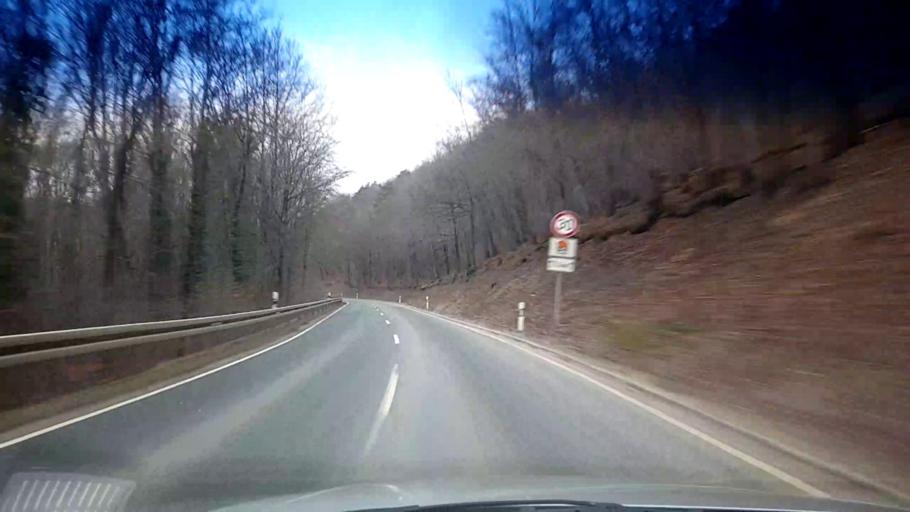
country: DE
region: Bavaria
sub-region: Upper Franconia
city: Wattendorf
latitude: 50.0505
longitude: 11.0897
